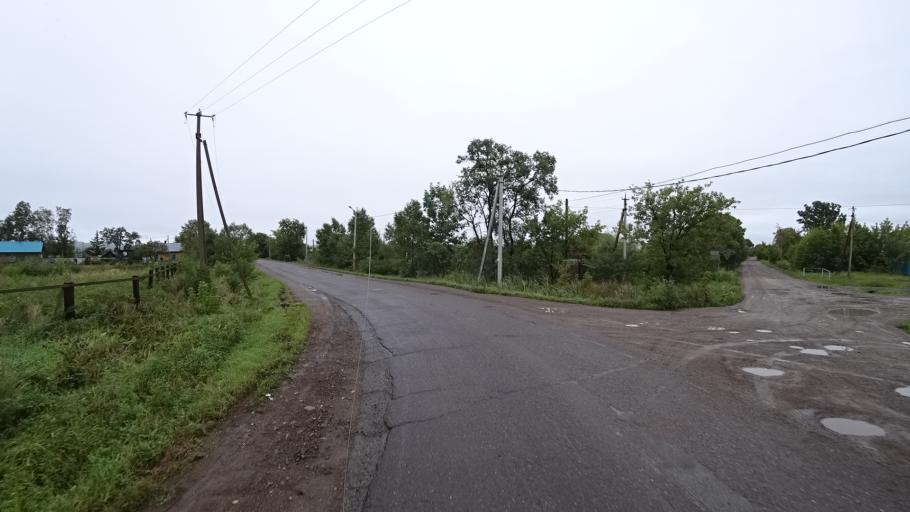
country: RU
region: Primorskiy
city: Monastyrishche
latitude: 44.1984
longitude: 132.4628
